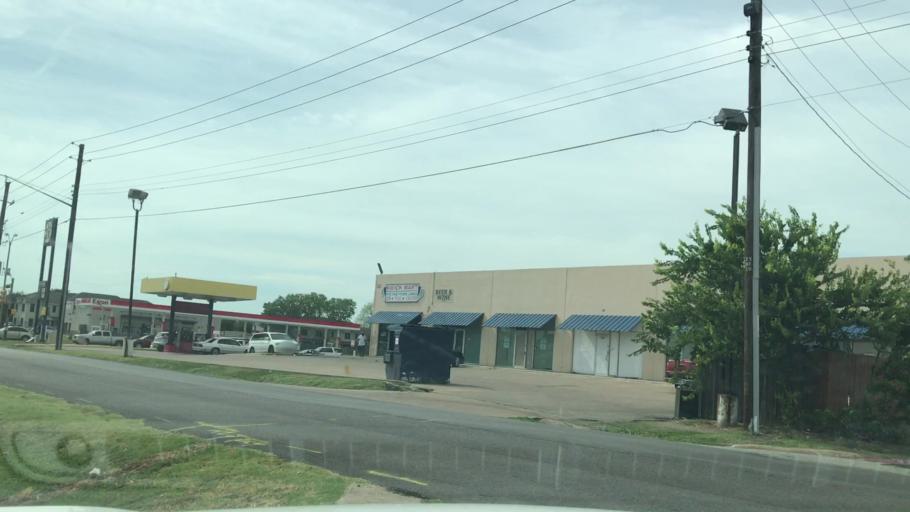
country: US
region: Texas
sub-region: Dallas County
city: Mesquite
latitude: 32.8070
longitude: -96.6673
